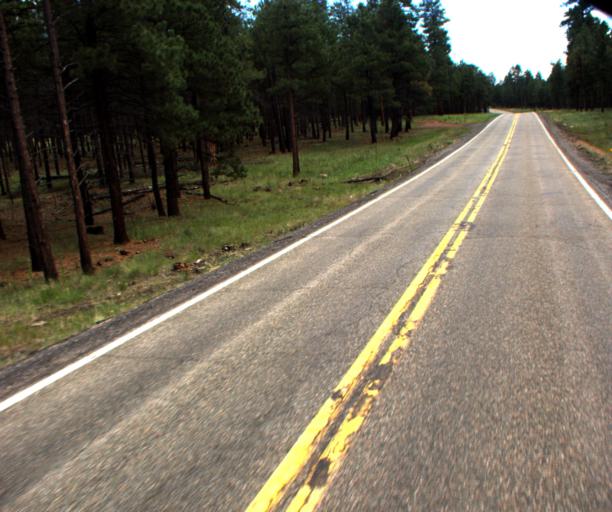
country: US
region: Arizona
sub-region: Coconino County
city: Parks
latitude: 35.3354
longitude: -111.7838
